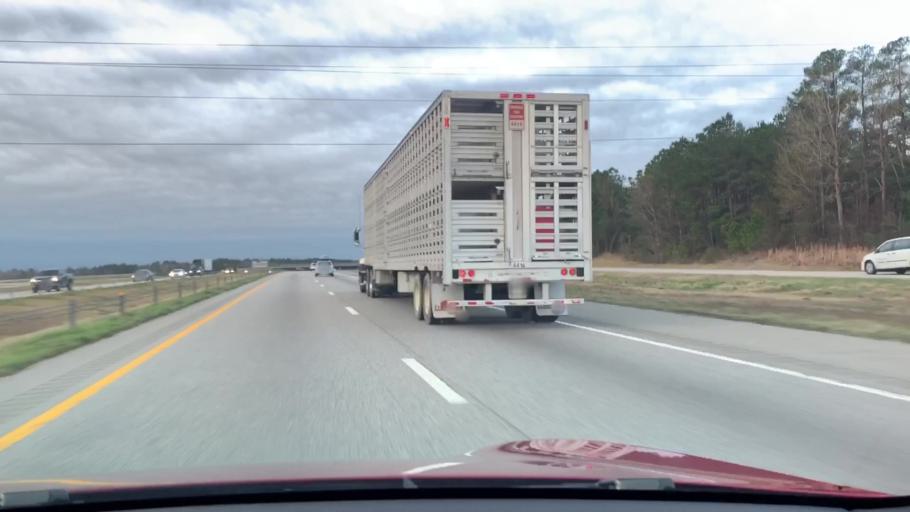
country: US
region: North Carolina
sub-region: Robeson County
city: Lumberton
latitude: 34.5987
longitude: -79.1057
